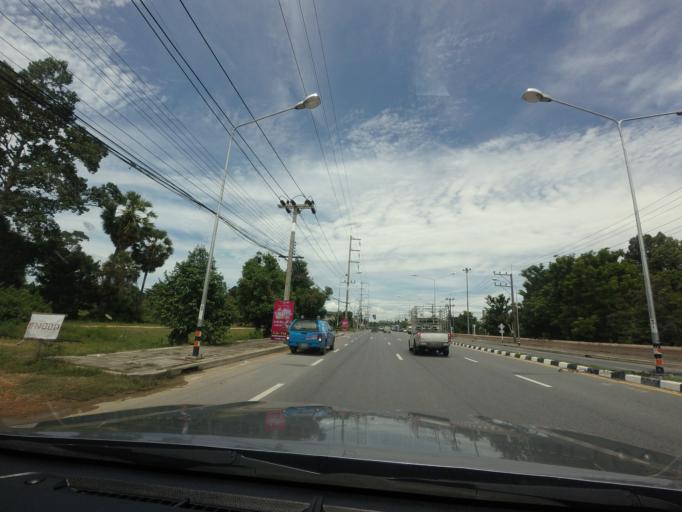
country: TH
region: Songkhla
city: Krasae Sin
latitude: 7.6028
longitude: 100.4006
